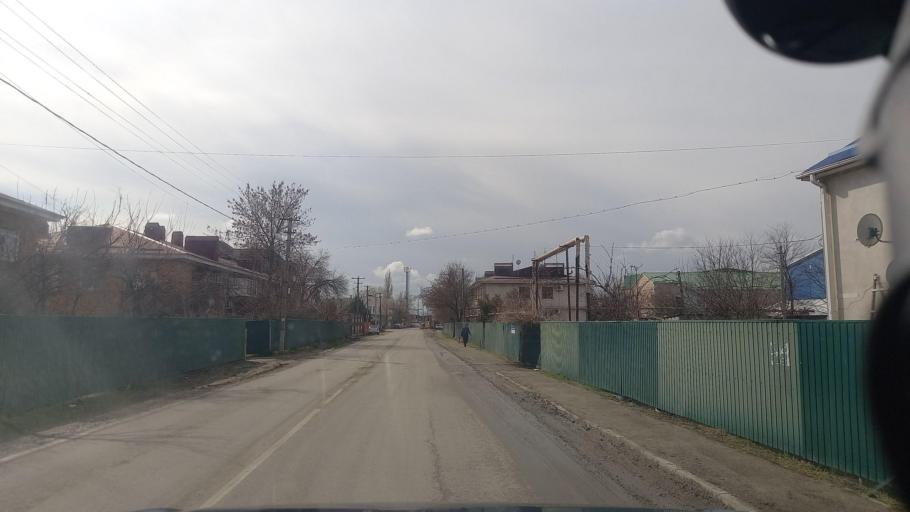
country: RU
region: Adygeya
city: Takhtamukay
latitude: 44.9254
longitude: 38.9929
